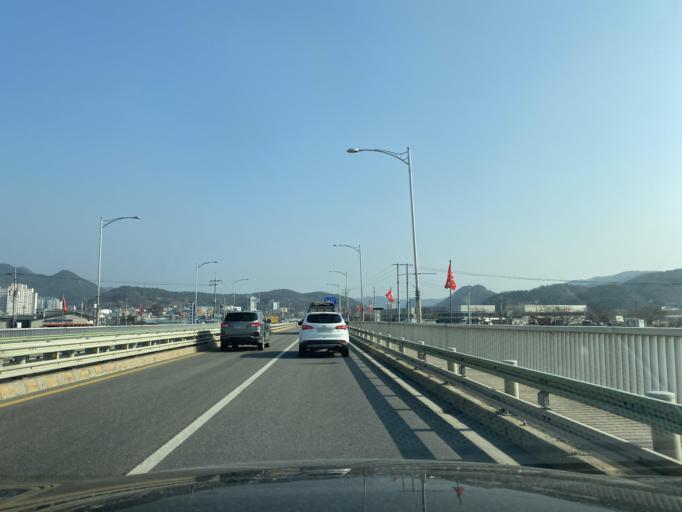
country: KR
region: Chungcheongnam-do
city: Yesan
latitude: 36.6839
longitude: 126.8217
